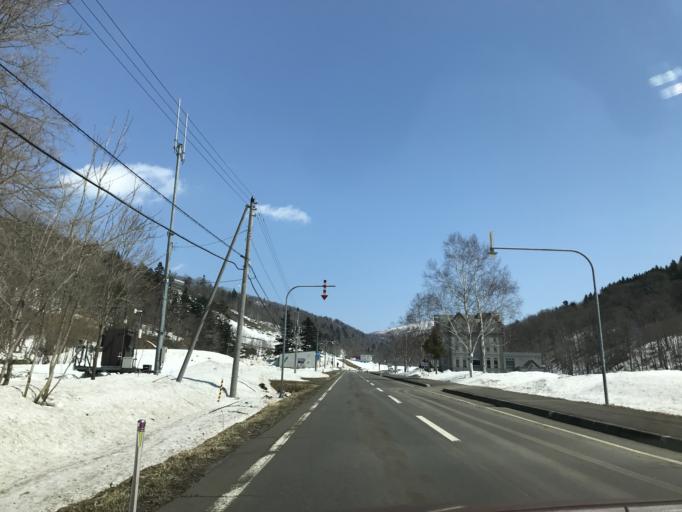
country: JP
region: Hokkaido
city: Nayoro
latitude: 44.4007
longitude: 142.5125
